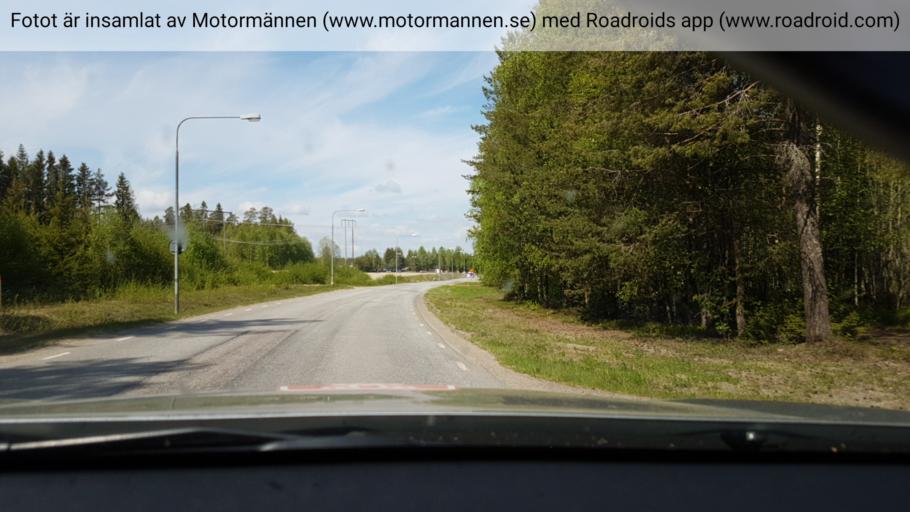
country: SE
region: Vaesterbotten
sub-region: Umea Kommun
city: Roback
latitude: 63.8176
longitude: 20.1793
